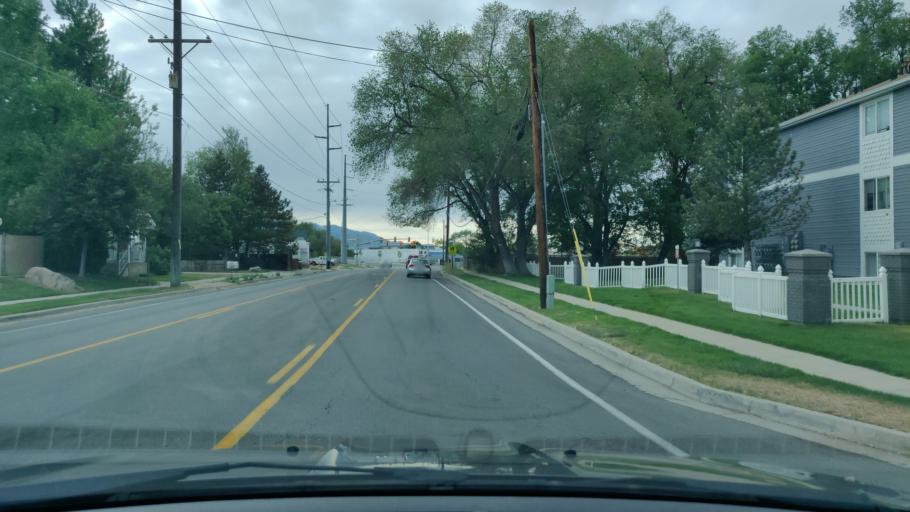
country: US
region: Utah
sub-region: Salt Lake County
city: Sandy City
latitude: 40.6195
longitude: -111.8638
